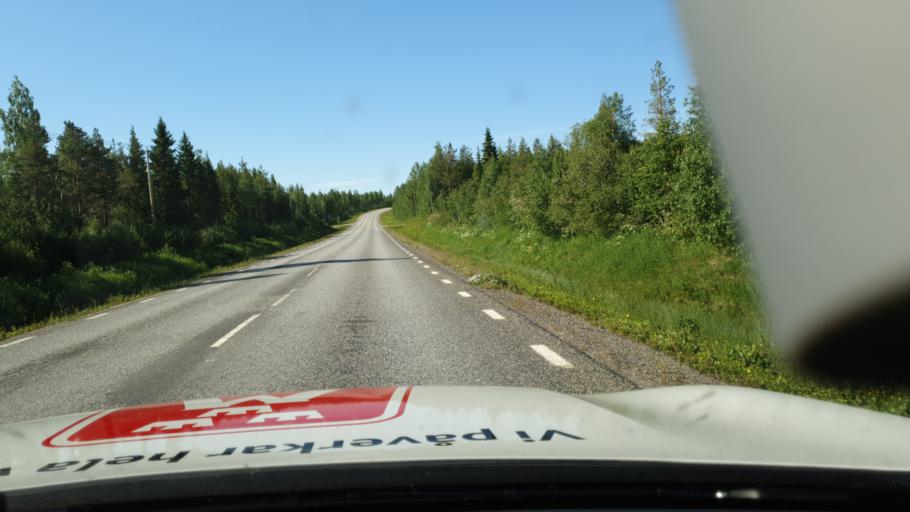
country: SE
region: Vaesterbotten
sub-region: Lycksele Kommun
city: Lycksele
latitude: 64.5468
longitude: 18.5063
